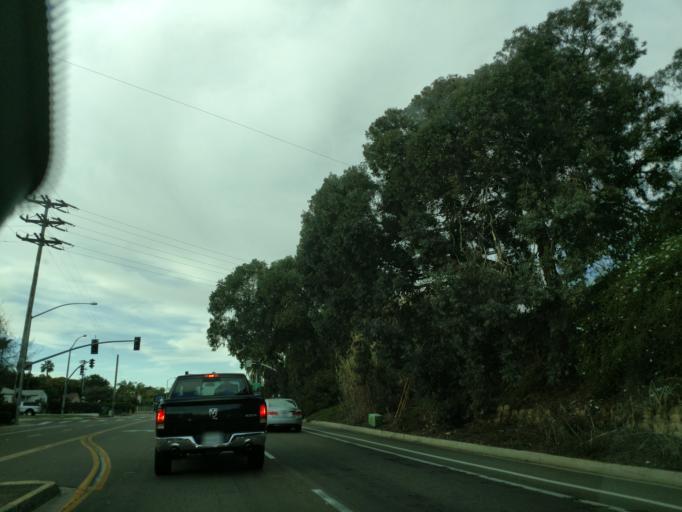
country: US
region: California
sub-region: San Diego County
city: Coronado
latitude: 32.7366
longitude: -117.2303
